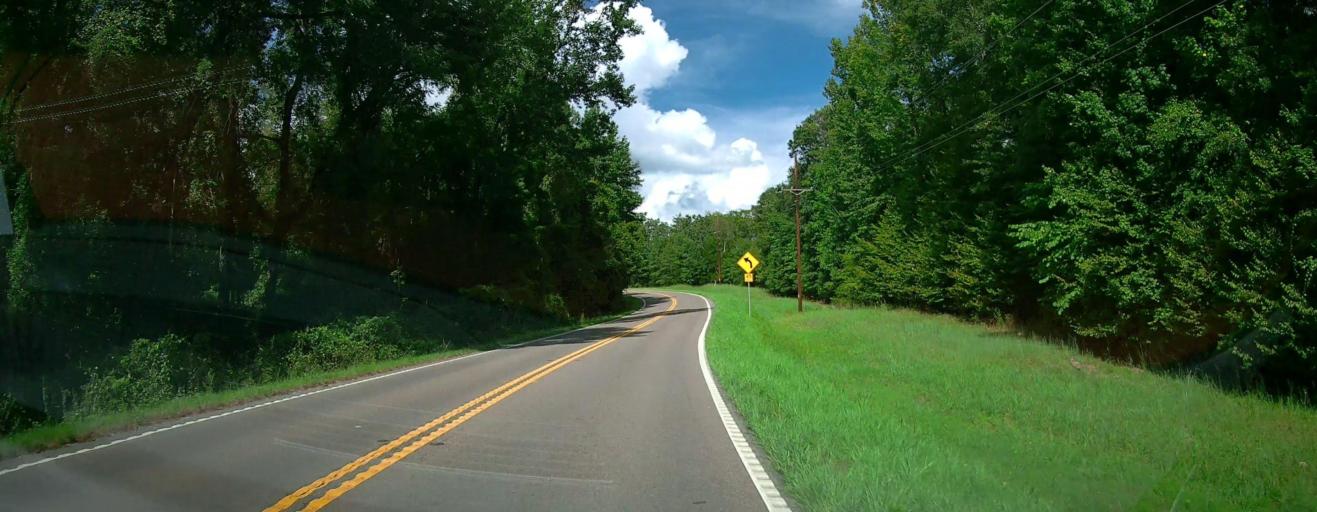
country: US
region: Georgia
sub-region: Talbot County
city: Talbotton
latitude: 32.6225
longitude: -84.4883
